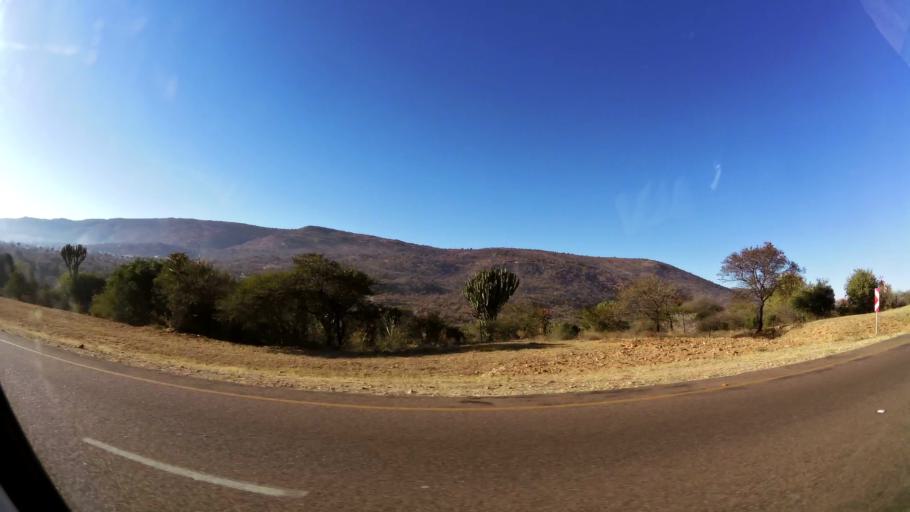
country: ZA
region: Limpopo
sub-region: Capricorn District Municipality
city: Mankoeng
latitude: -23.9440
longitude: 29.8059
